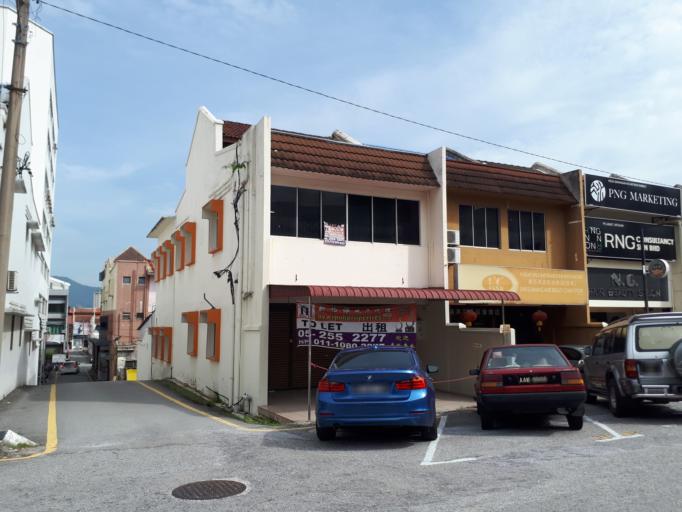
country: MY
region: Perak
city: Ipoh
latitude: 4.5988
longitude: 101.0879
